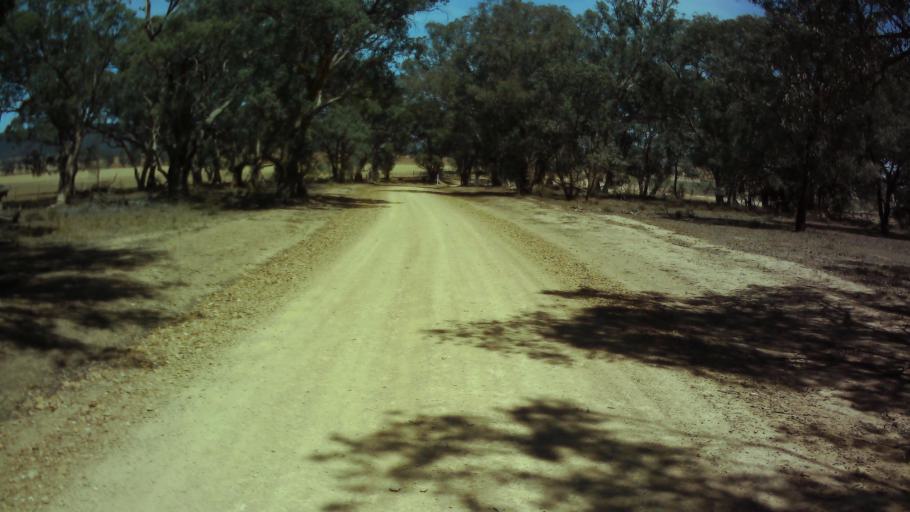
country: AU
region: New South Wales
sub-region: Weddin
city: Grenfell
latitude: -33.9687
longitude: 148.1403
